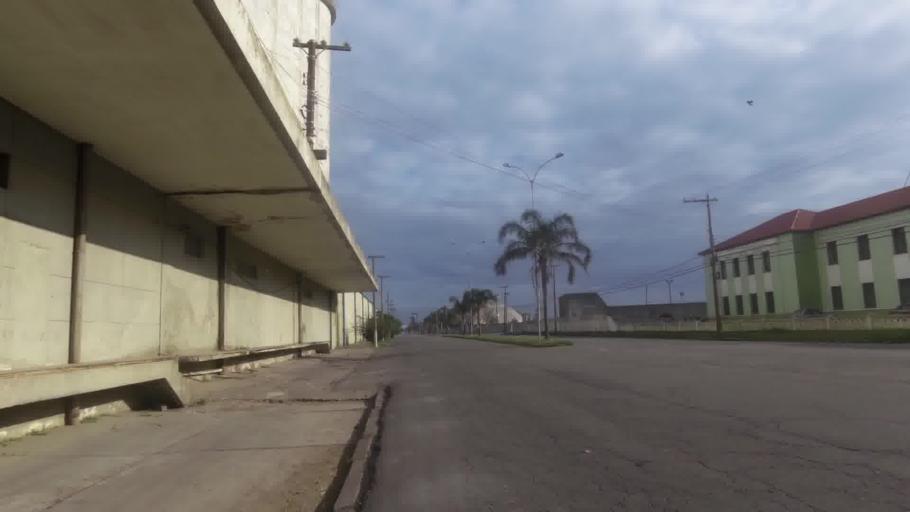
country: BR
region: Rio Grande do Sul
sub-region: Rio Grande
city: Rio Grande
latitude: -32.0353
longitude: -52.0790
